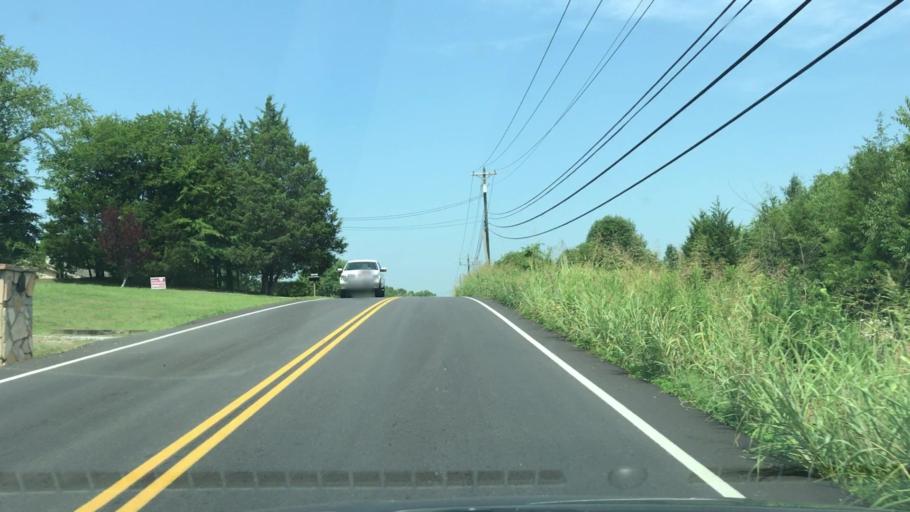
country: US
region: Tennessee
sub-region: Wilson County
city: Rural Hill
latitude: 36.1255
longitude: -86.5159
